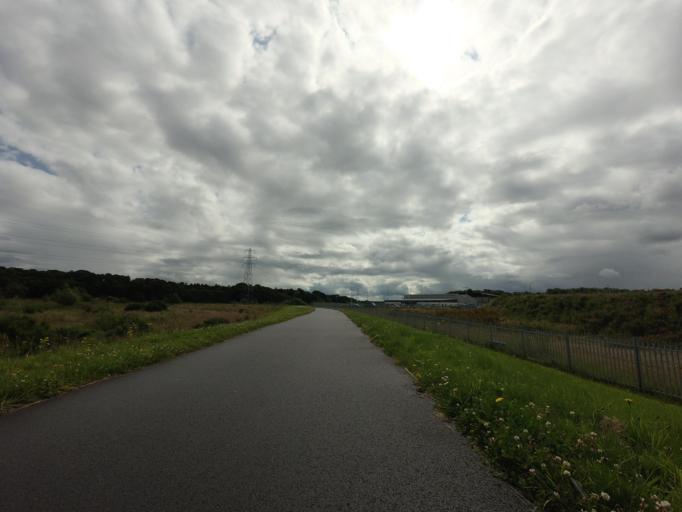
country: GB
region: Scotland
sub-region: Moray
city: Elgin
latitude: 57.6509
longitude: -3.2896
